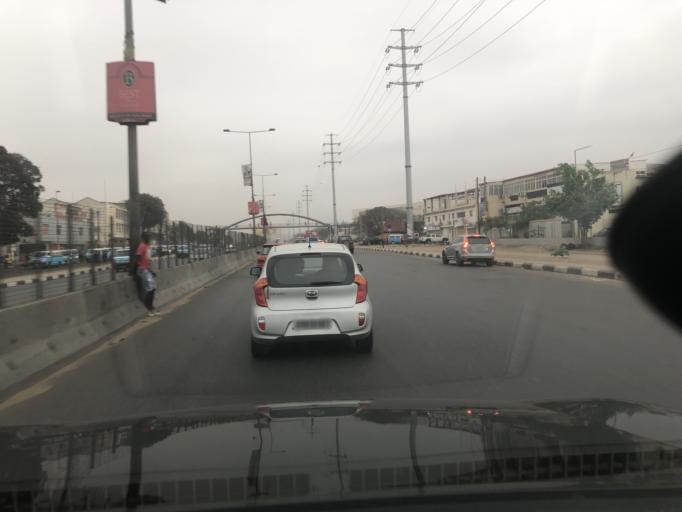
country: AO
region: Luanda
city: Luanda
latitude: -8.8380
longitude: 13.2620
